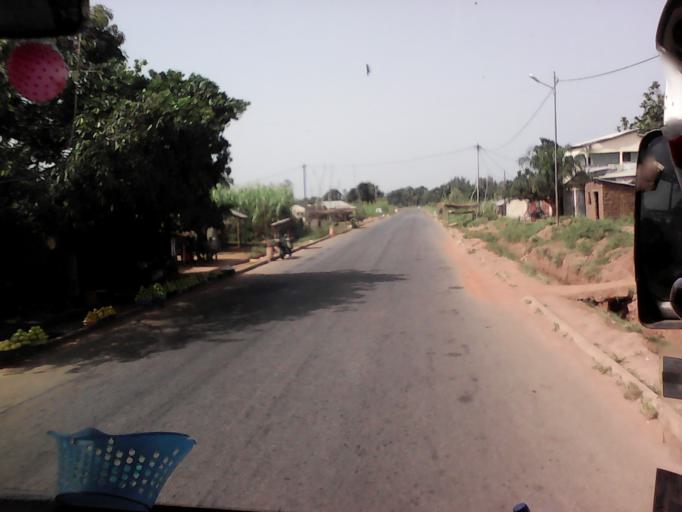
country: TG
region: Centrale
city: Sokode
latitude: 8.9232
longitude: 1.1106
